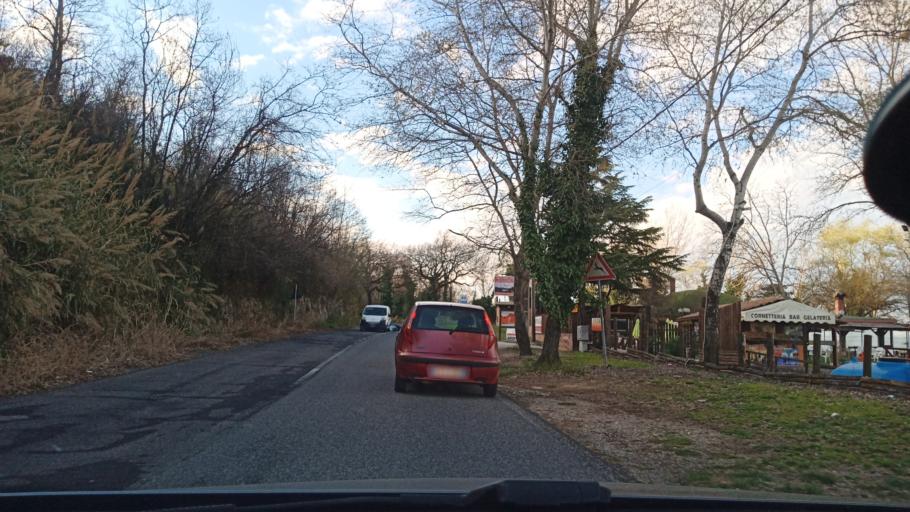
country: IT
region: Latium
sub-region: Citta metropolitana di Roma Capitale
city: Nazzano
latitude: 42.2142
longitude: 12.6009
